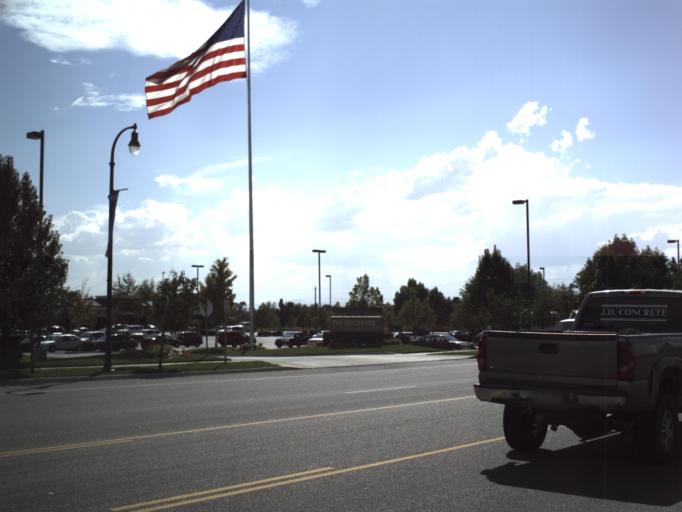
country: US
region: Utah
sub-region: Utah County
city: Orem
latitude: 40.3120
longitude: -111.6721
